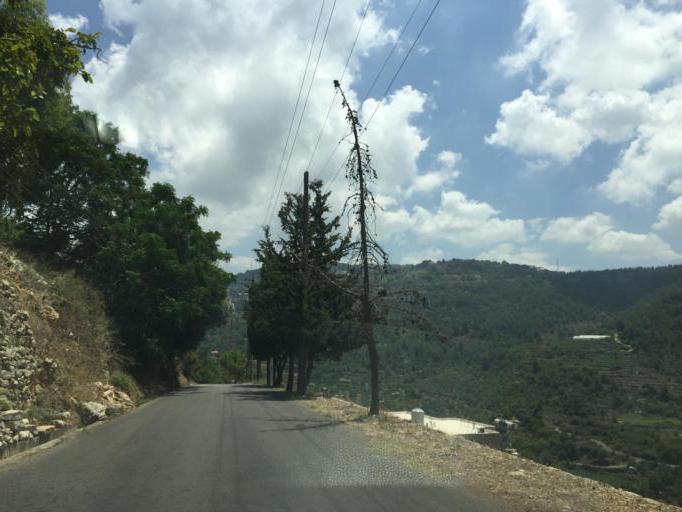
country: LB
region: Mont-Liban
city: Beit ed Dine
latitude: 33.6959
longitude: 35.5662
